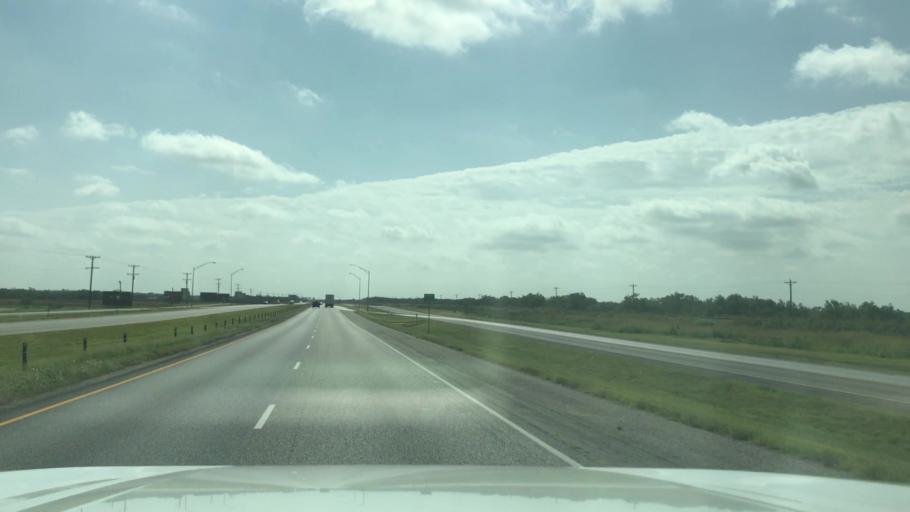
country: US
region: Texas
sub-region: Taylor County
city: Merkel
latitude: 32.4668
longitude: -99.9829
